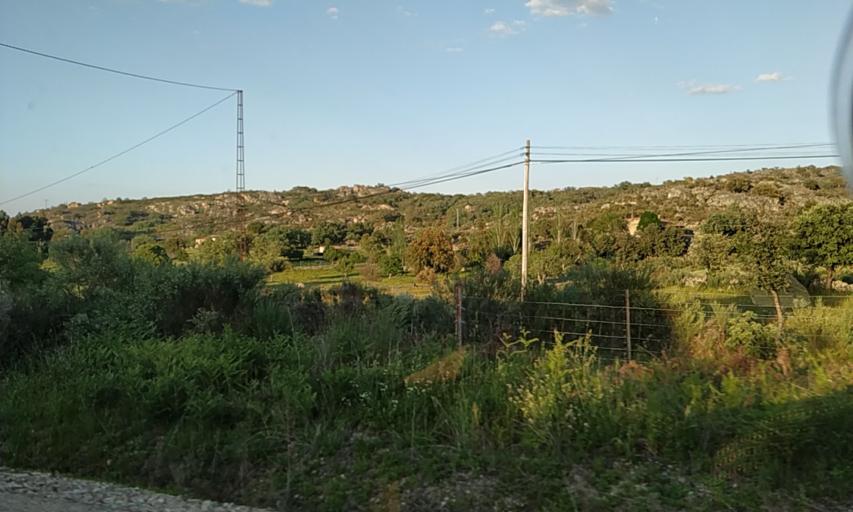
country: PT
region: Portalegre
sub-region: Portalegre
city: Sao Juliao
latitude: 39.3579
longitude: -7.2751
